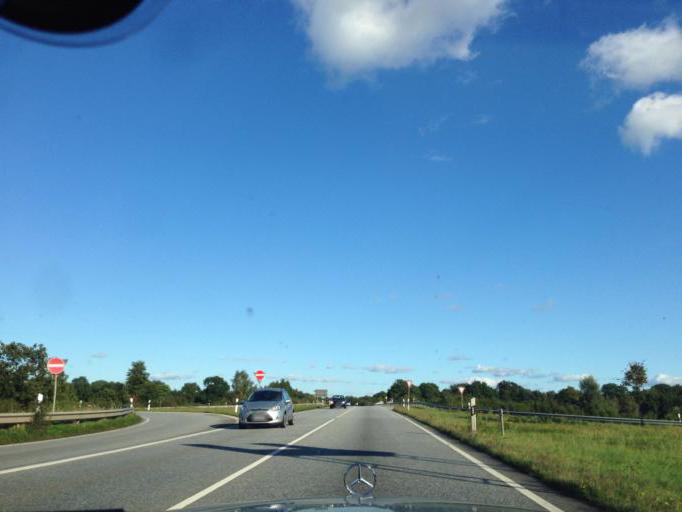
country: DE
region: Schleswig-Holstein
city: Neumunster
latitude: 54.0417
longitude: 9.9634
